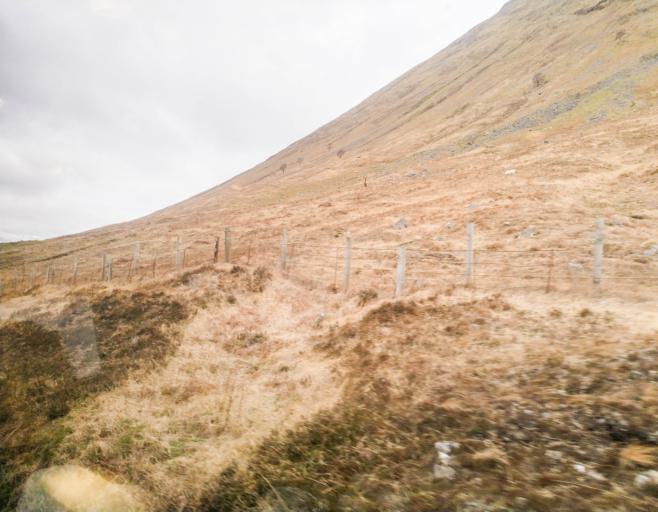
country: GB
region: Scotland
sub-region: Argyll and Bute
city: Garelochhead
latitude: 56.4892
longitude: -4.7271
